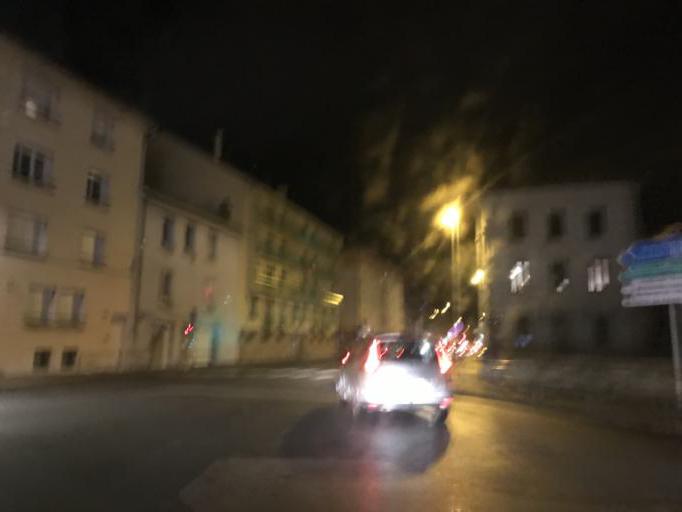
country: FR
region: Rhone-Alpes
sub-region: Departement de l'Ain
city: Bourg-en-Bresse
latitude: 46.2058
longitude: 5.2347
